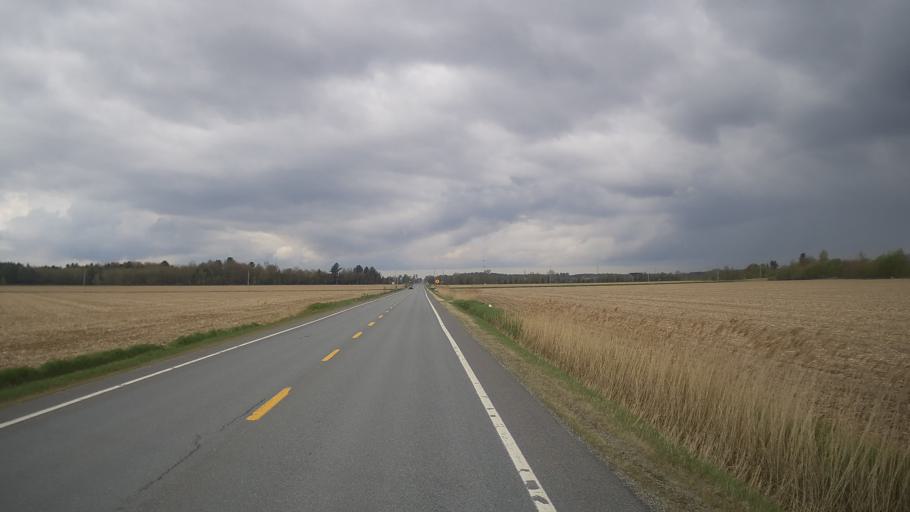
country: CA
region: Quebec
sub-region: Monteregie
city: Farnham
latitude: 45.2524
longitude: -72.9052
